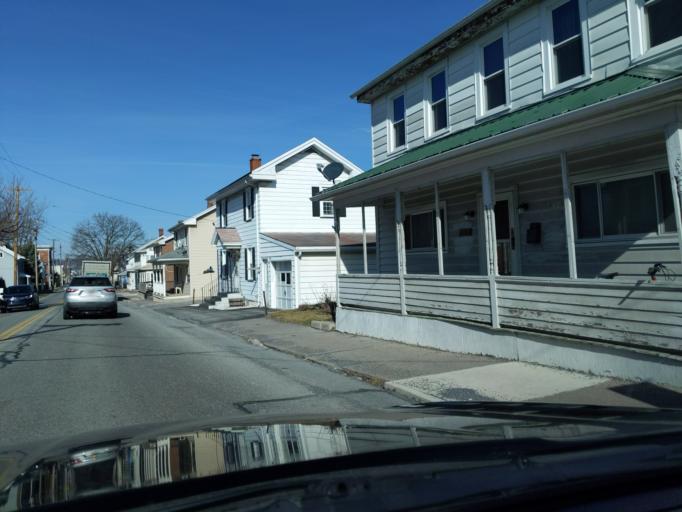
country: US
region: Pennsylvania
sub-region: Blair County
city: Martinsburg
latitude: 40.3101
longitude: -78.3210
